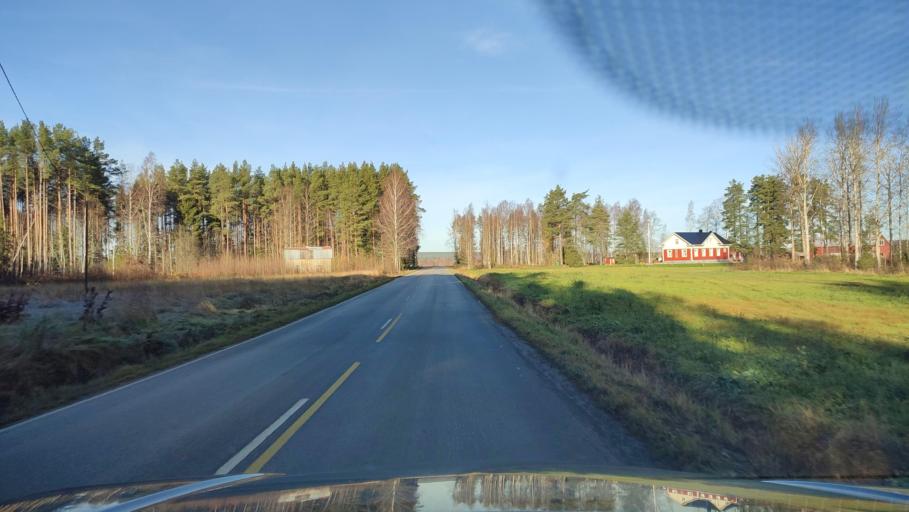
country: FI
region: Southern Ostrobothnia
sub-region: Suupohja
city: Karijoki
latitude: 62.2646
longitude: 21.7286
